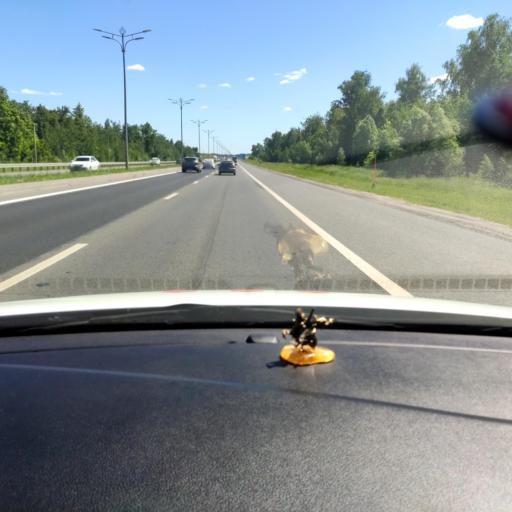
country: RU
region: Tatarstan
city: Stolbishchi
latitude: 55.7074
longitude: 49.2192
